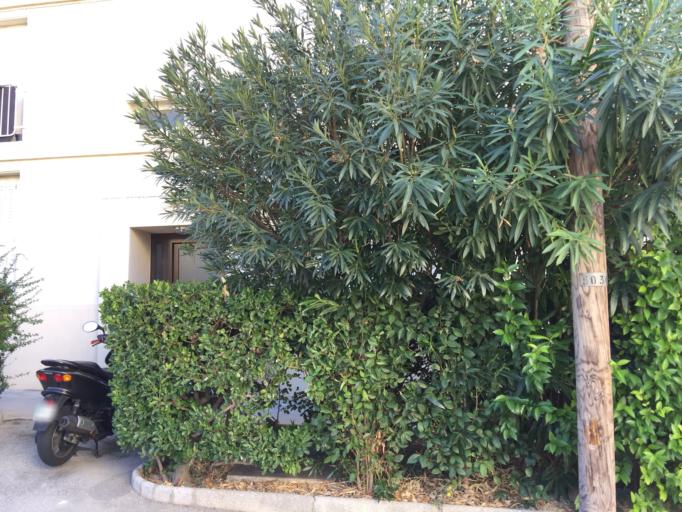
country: FR
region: Provence-Alpes-Cote d'Azur
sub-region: Departement des Bouches-du-Rhone
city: Marseille 10
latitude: 43.2745
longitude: 5.4108
